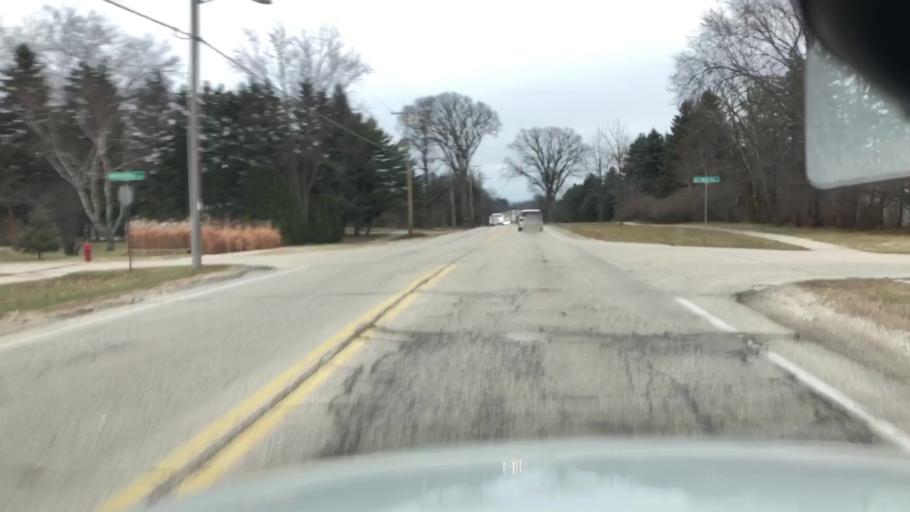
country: US
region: Wisconsin
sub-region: Waukesha County
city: Brookfield
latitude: 43.0611
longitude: -88.1355
